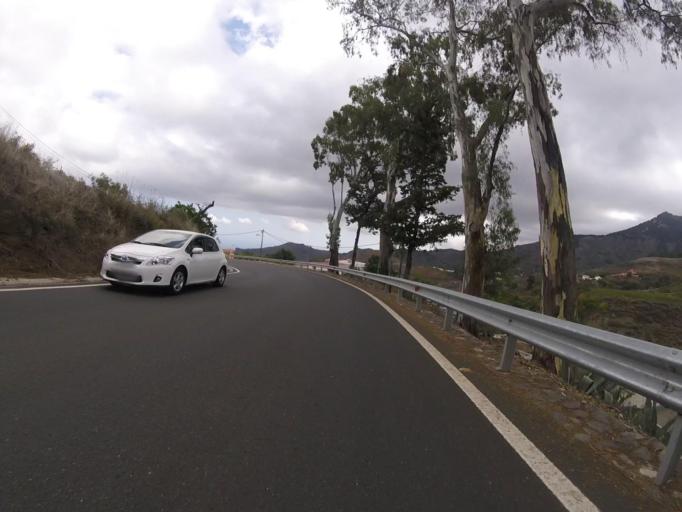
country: ES
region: Canary Islands
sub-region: Provincia de Las Palmas
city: Vega de San Mateo
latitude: 28.0043
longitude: -15.5582
